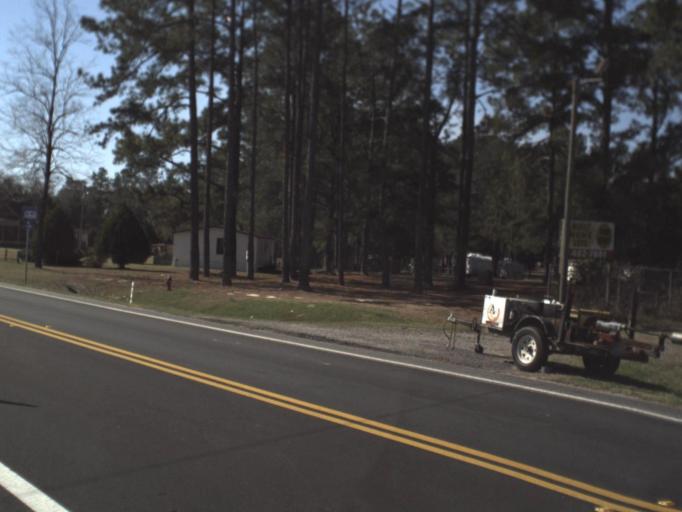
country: US
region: Florida
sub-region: Jackson County
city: Marianna
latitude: 30.7099
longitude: -85.1852
